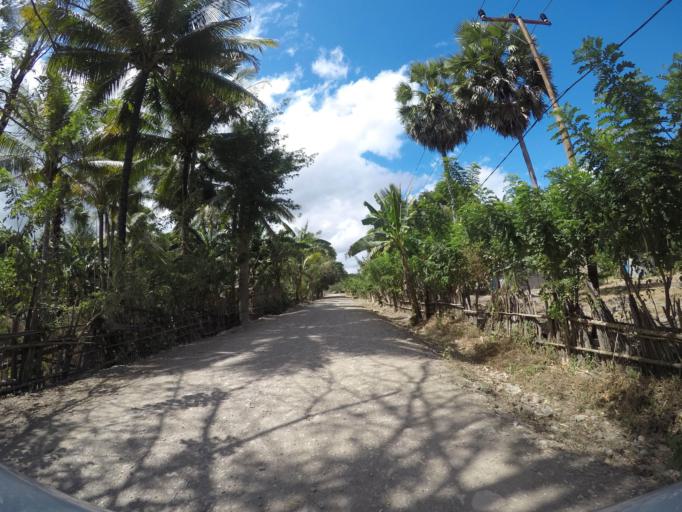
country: TL
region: Lautem
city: Lospalos
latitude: -8.4849
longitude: 126.8187
